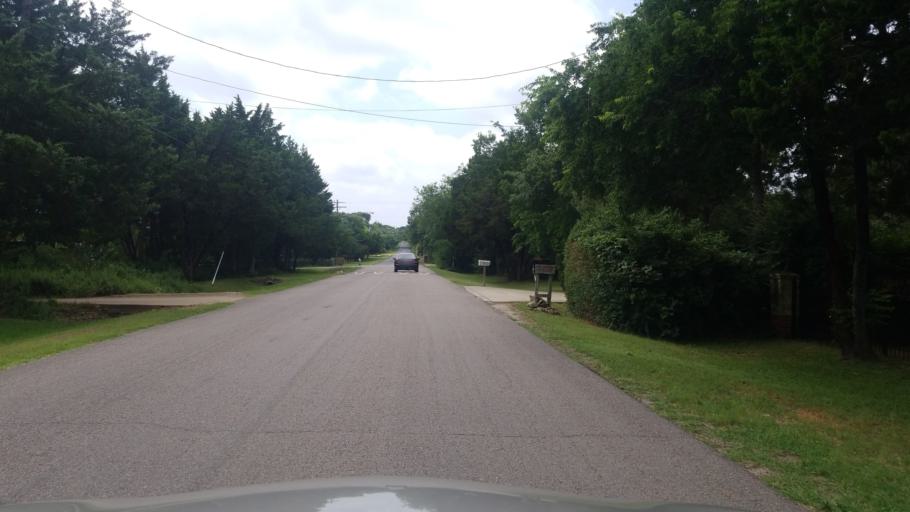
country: US
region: Texas
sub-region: Dallas County
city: Duncanville
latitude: 32.6823
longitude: -96.9341
